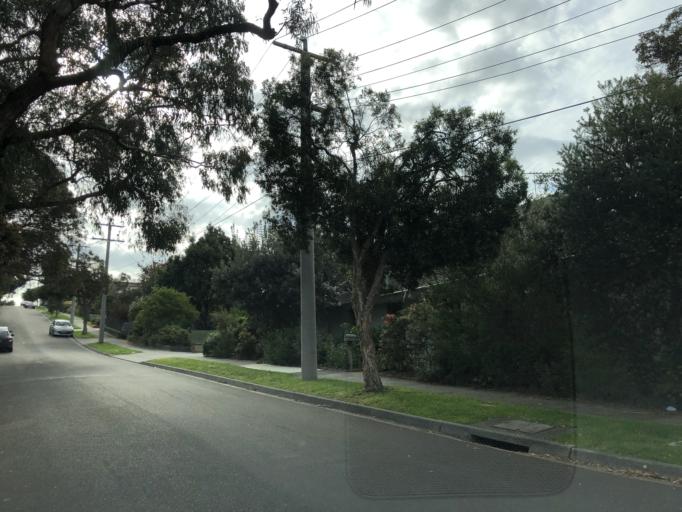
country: AU
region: Victoria
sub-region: Knox
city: Rowville
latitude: -37.9369
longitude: 145.2248
